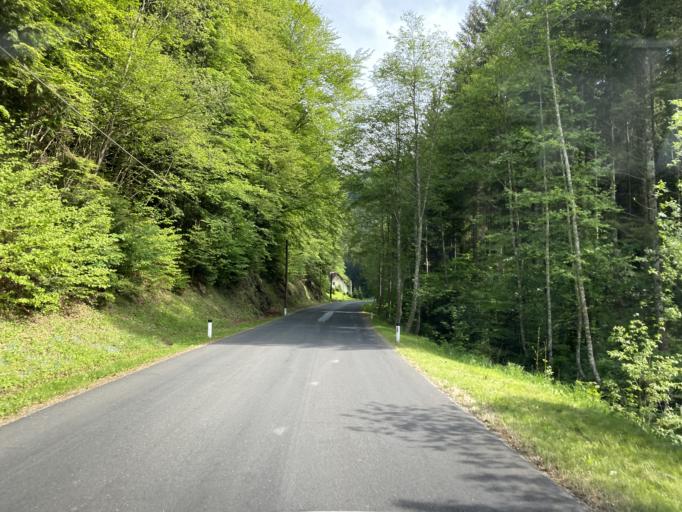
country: AT
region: Styria
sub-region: Politischer Bezirk Weiz
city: Koglhof
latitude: 47.3223
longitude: 15.6360
